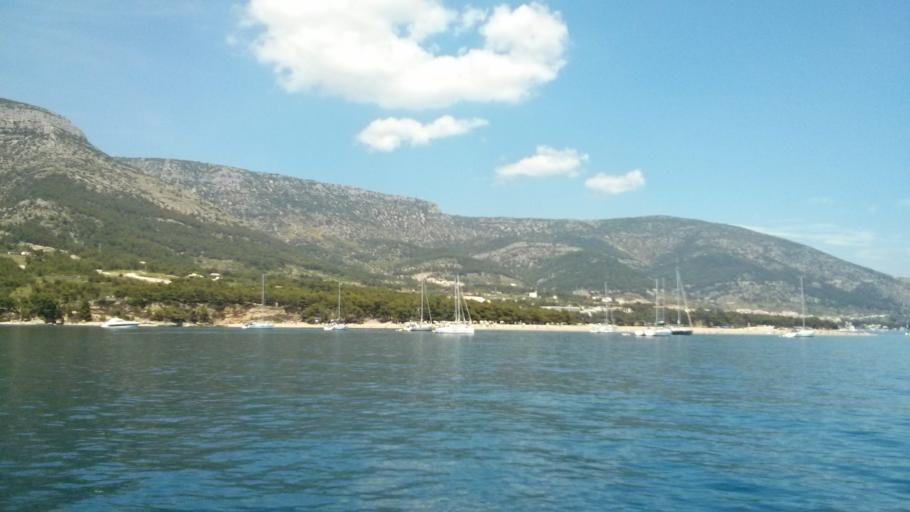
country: HR
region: Splitsko-Dalmatinska
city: Bol
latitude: 43.2547
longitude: 16.6287
